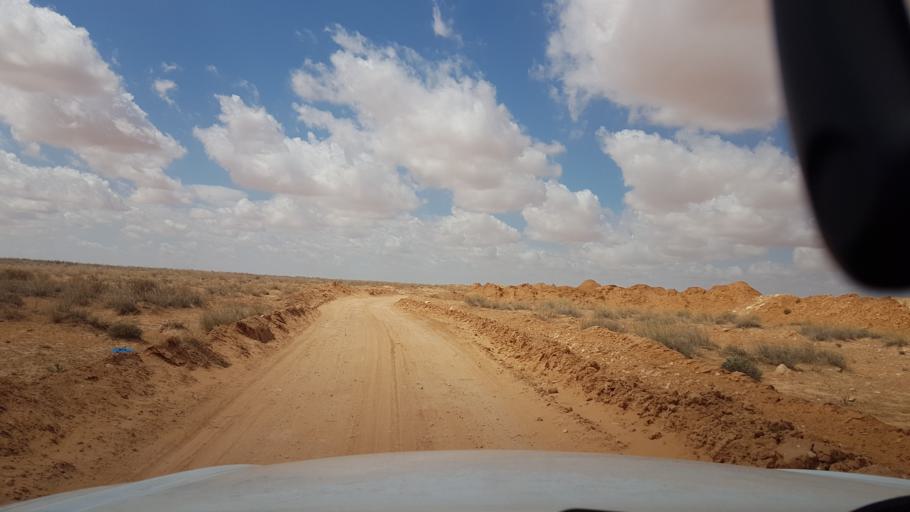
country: TN
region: Madanin
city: Medenine
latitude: 33.2676
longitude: 10.5849
